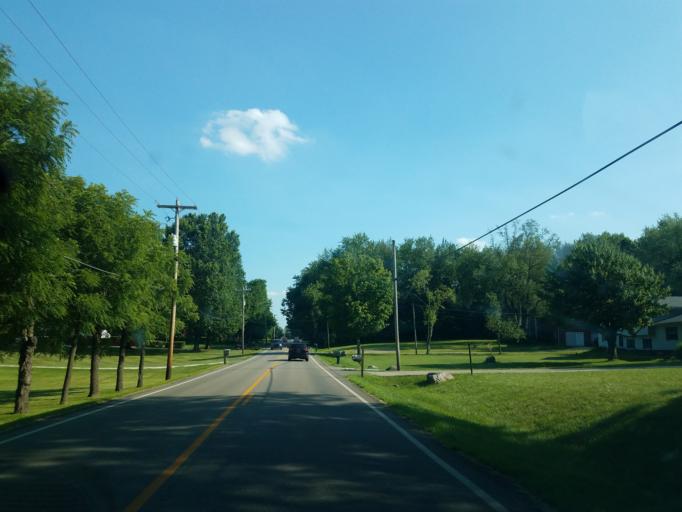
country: US
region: Ohio
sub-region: Stark County
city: Greentown
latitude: 40.9326
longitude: -81.4285
